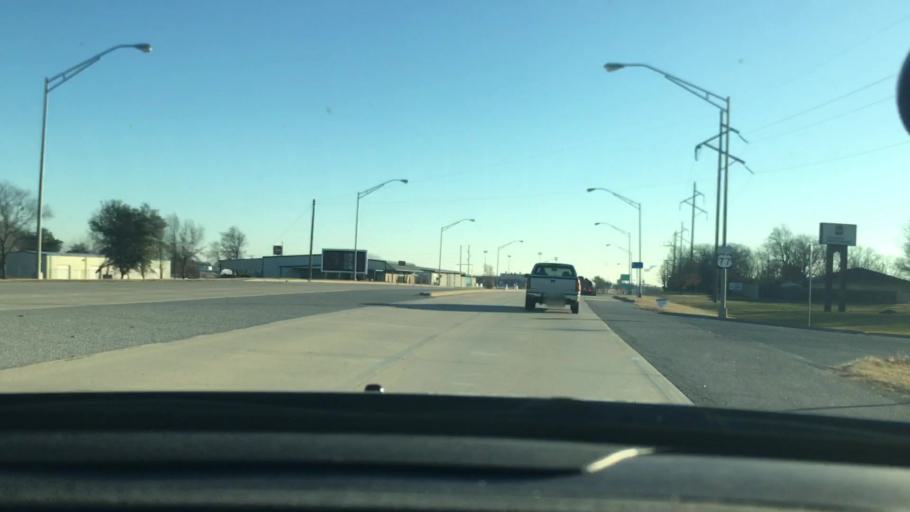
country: US
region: Oklahoma
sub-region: Carter County
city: Ardmore
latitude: 34.2027
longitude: -97.1473
